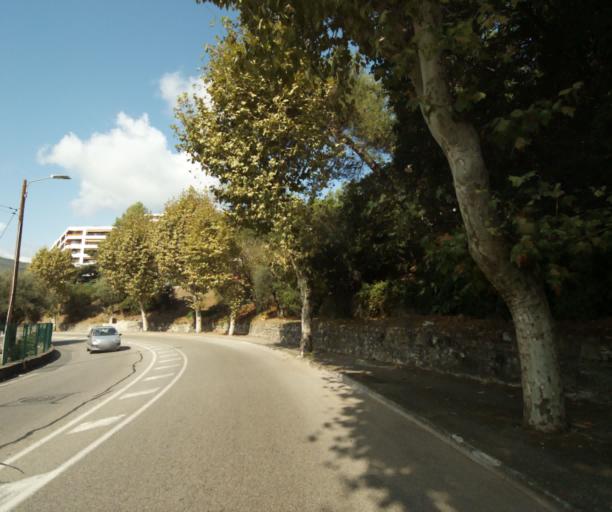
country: FR
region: Provence-Alpes-Cote d'Azur
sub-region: Departement des Alpes-Maritimes
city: Drap
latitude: 43.7477
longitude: 7.3210
